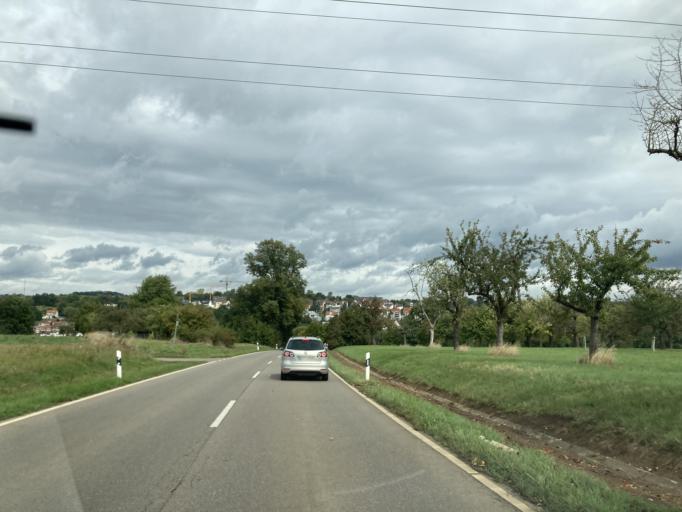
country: DE
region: Baden-Wuerttemberg
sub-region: Regierungsbezirk Stuttgart
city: Neuhausen auf den Fildern
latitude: 48.7032
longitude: 9.2648
